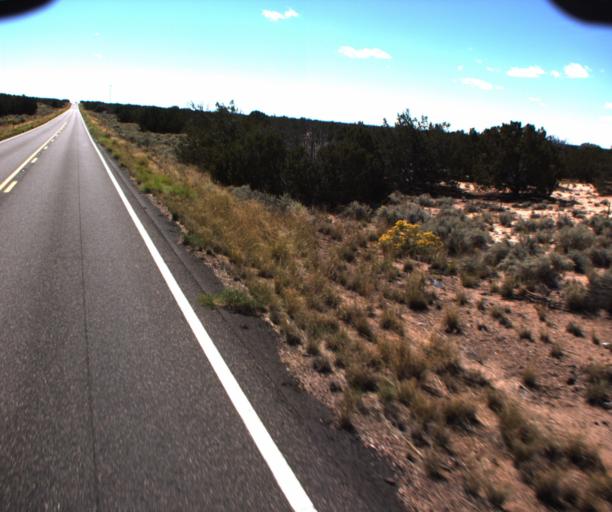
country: US
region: Arizona
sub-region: Apache County
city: Saint Johns
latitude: 34.8582
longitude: -109.2377
